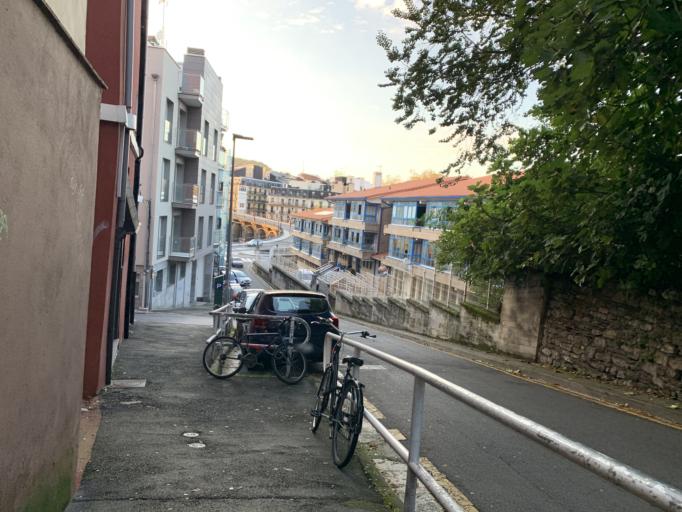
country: ES
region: Basque Country
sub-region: Provincia de Guipuzcoa
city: San Sebastian
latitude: 43.3205
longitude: -1.9727
